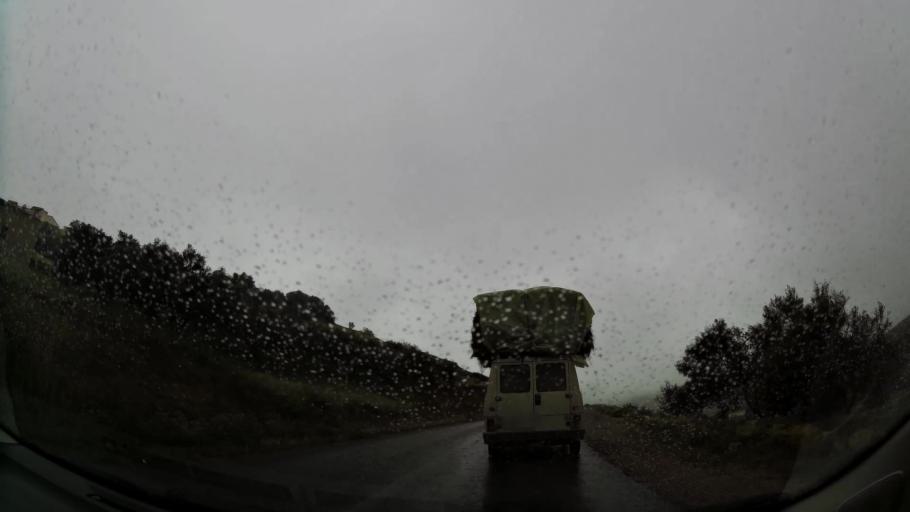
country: MA
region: Oriental
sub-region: Nador
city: Boudinar
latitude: 35.0923
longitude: -3.5257
